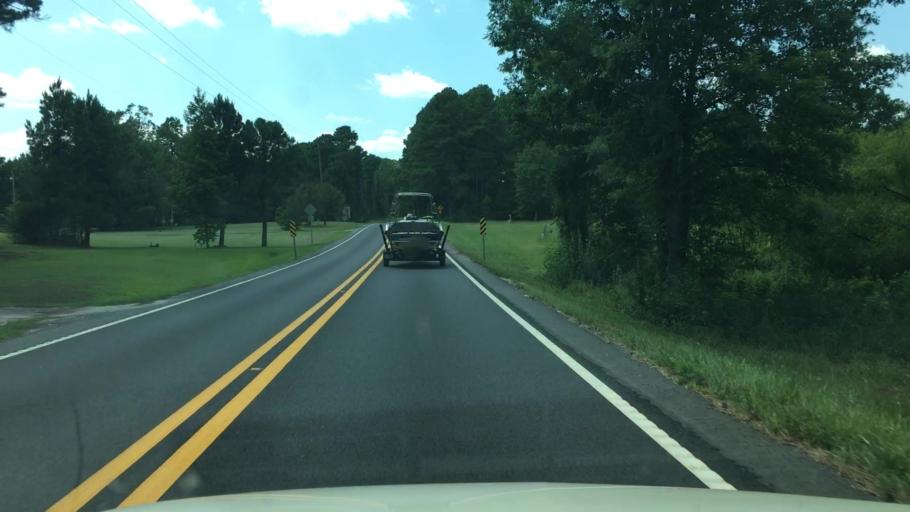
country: US
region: Arkansas
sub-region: Garland County
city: Lake Hamilton
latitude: 34.2781
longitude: -93.1534
